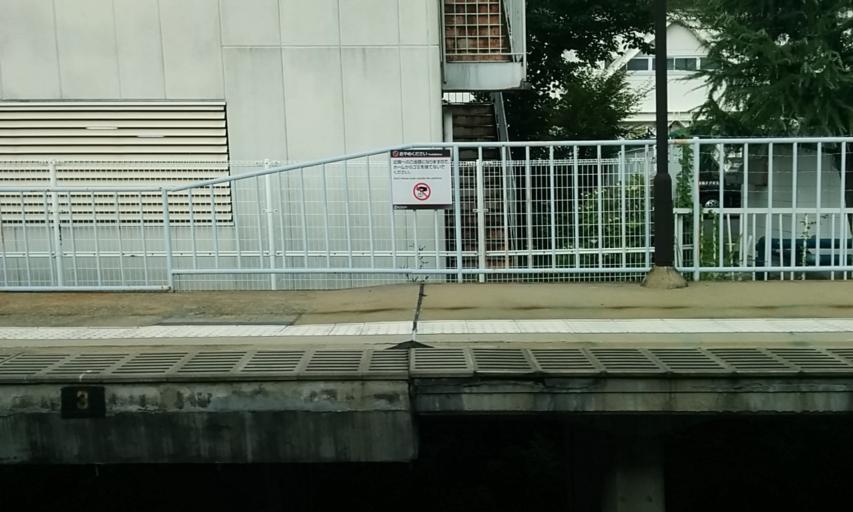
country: JP
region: Kyoto
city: Uji
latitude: 34.9266
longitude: 135.7960
